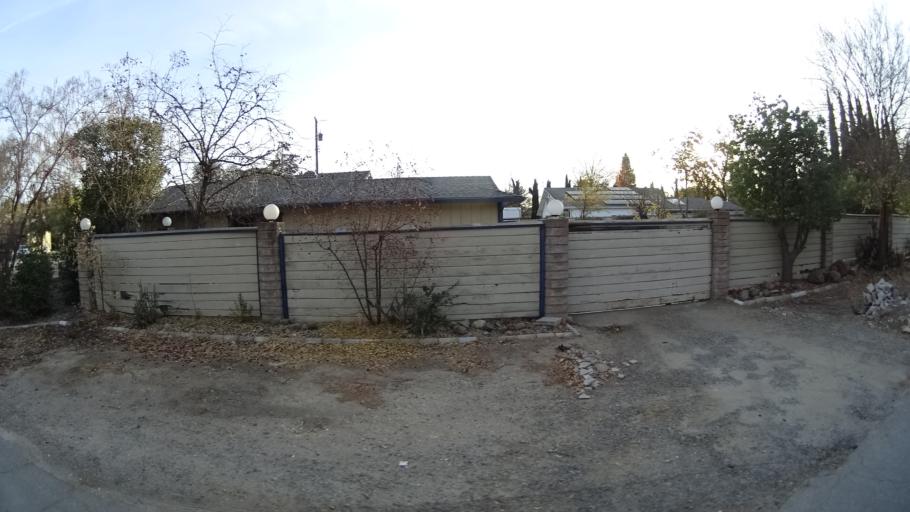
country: US
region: California
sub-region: Sacramento County
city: Citrus Heights
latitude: 38.7183
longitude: -121.2789
